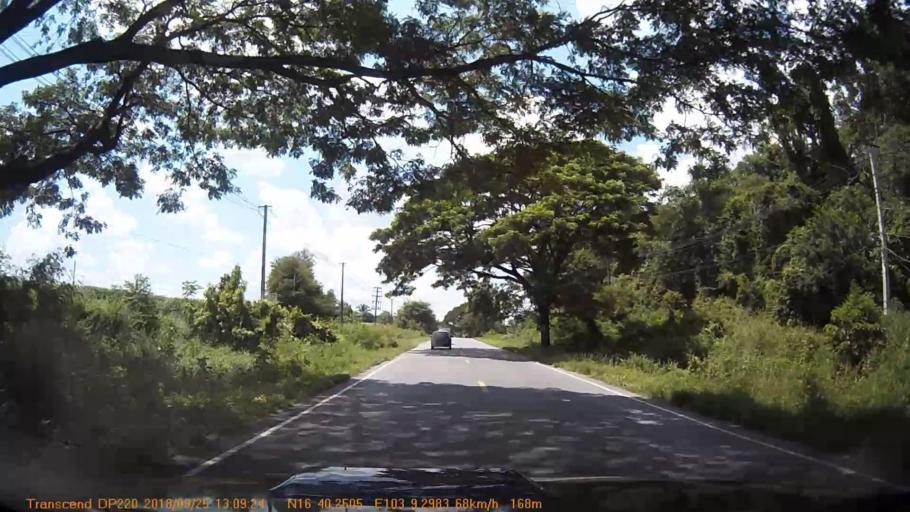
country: TH
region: Khon Kaen
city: Kranuan
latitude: 16.6708
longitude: 103.1550
